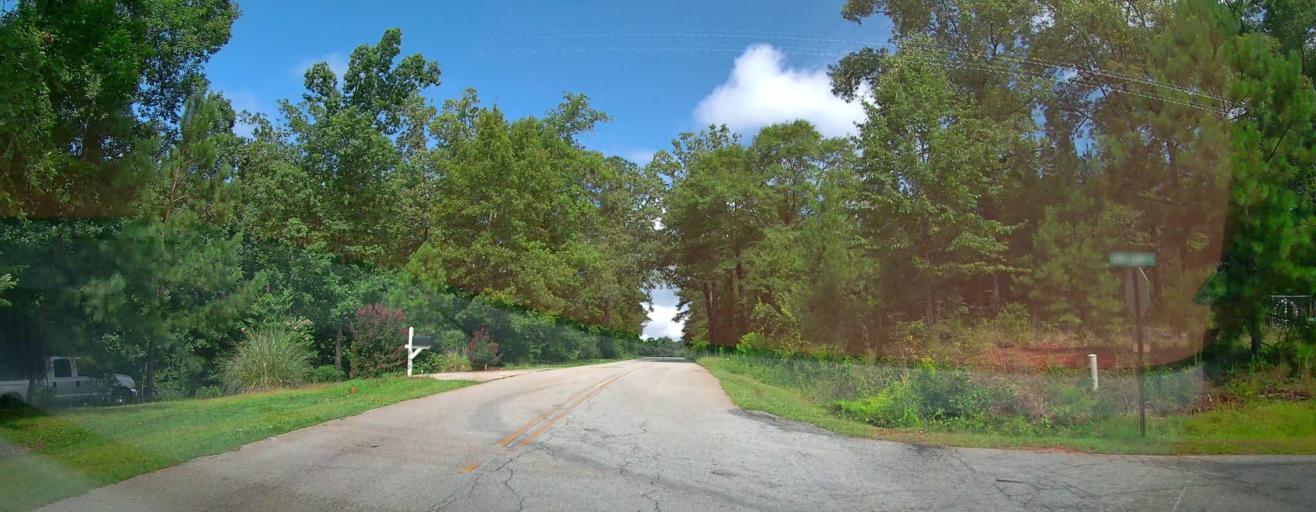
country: US
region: Georgia
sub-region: Peach County
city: Byron
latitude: 32.6612
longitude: -83.7756
